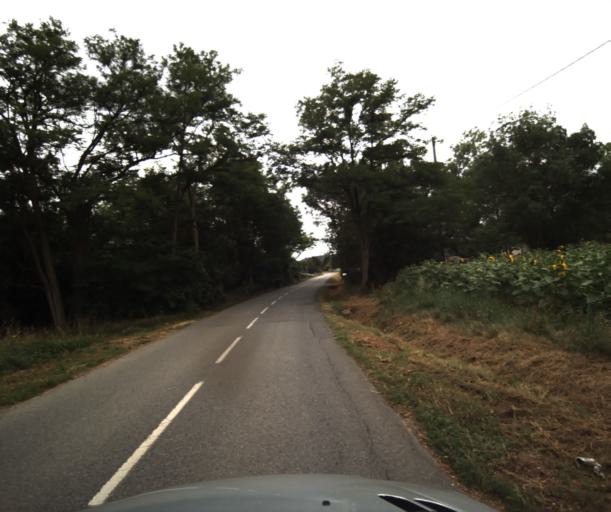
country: FR
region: Midi-Pyrenees
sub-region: Departement de la Haute-Garonne
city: Labarthe-sur-Leze
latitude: 43.4512
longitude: 1.4077
